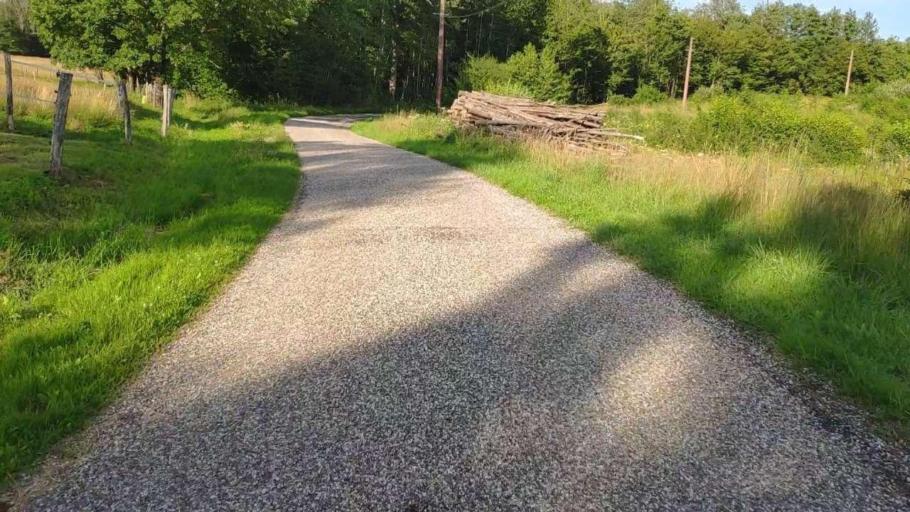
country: FR
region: Franche-Comte
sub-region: Departement du Jura
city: Bletterans
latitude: 46.7955
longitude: 5.4846
